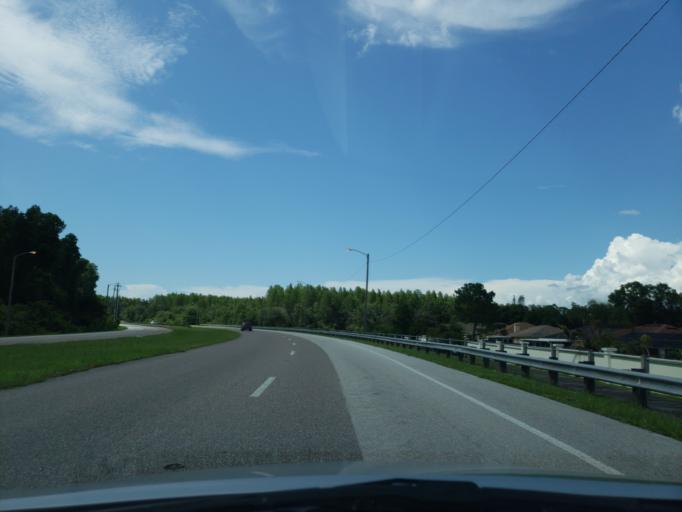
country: US
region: Florida
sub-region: Hillsborough County
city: Carrollwood Village
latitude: 28.0494
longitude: -82.5419
